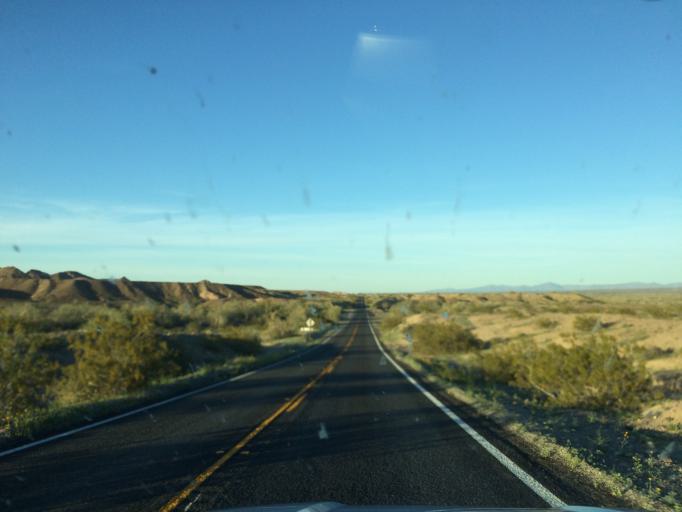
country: US
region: California
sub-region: Riverside County
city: Mesa Verde
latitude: 33.3101
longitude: -114.7389
